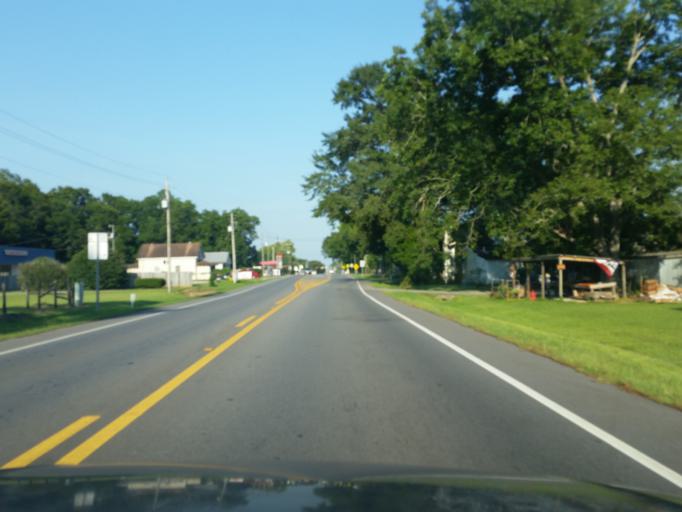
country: US
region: Alabama
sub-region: Baldwin County
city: Elberta
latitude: 30.4143
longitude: -87.6033
